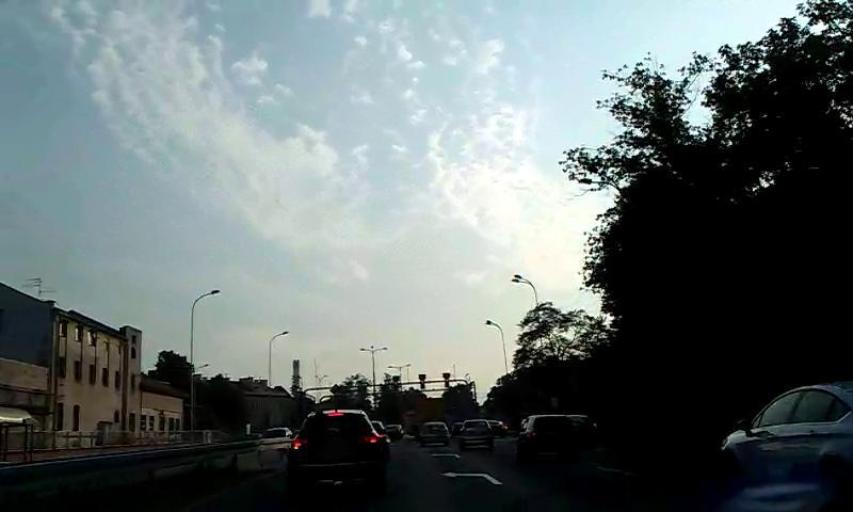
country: PL
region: Lublin Voivodeship
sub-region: Powiat lubelski
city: Lublin
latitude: 51.2238
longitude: 22.5770
